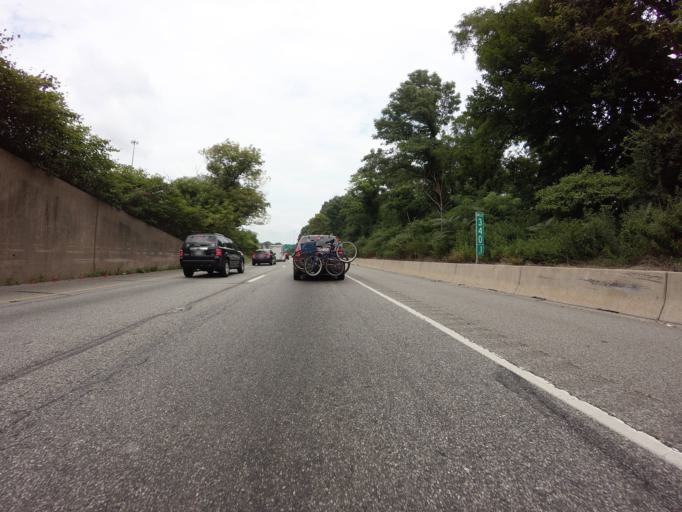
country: US
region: Pennsylvania
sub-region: Montgomery County
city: Bala-Cynwyd
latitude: 40.0062
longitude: -75.1970
